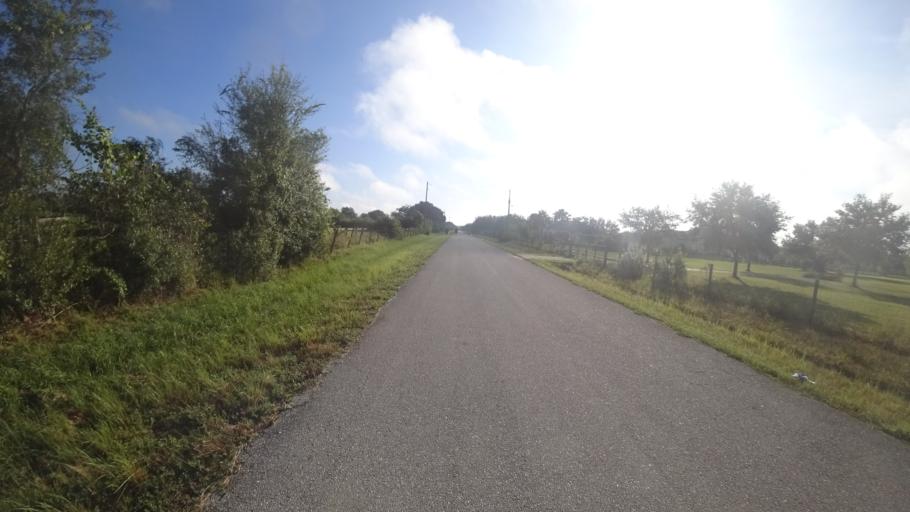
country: US
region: Florida
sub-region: Sarasota County
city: The Meadows
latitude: 27.4165
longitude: -82.3106
